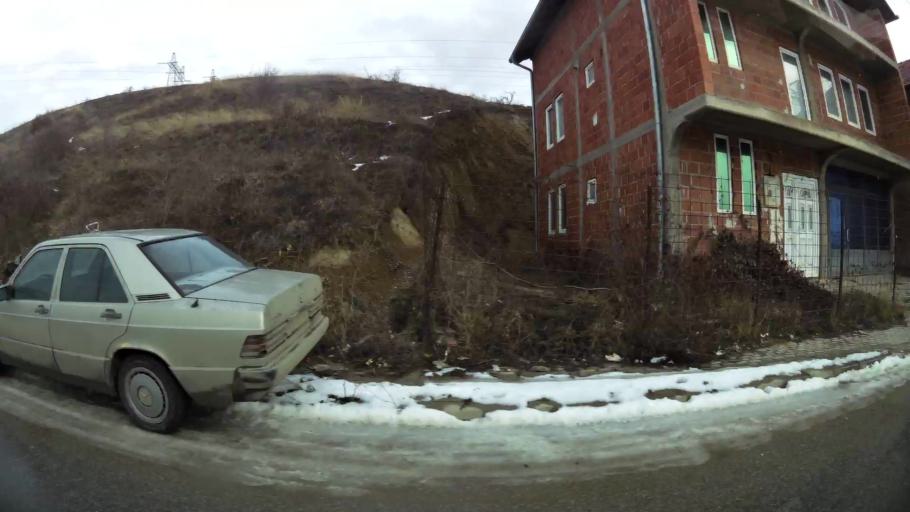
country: XK
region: Pristina
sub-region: Komuna e Prishtines
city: Pristina
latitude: 42.6920
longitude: 21.1752
